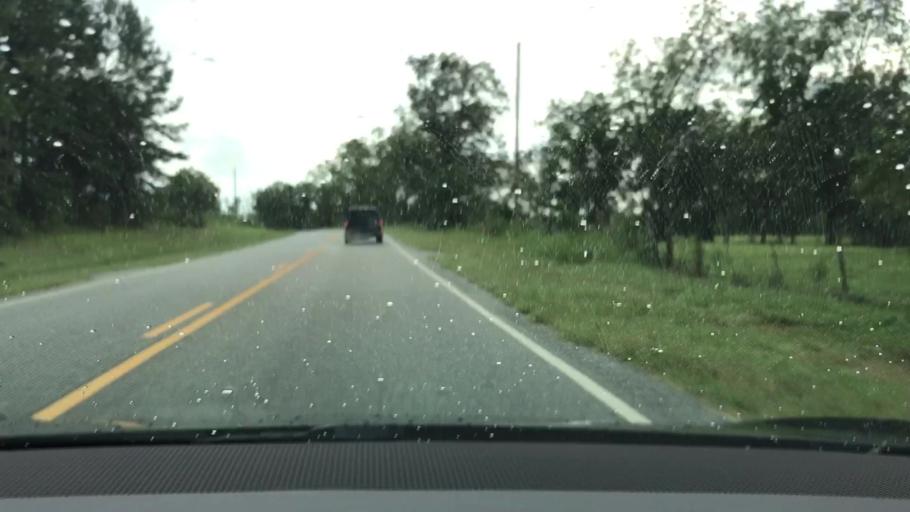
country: US
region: Alabama
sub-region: Geneva County
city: Samson
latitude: 31.0979
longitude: -86.1118
